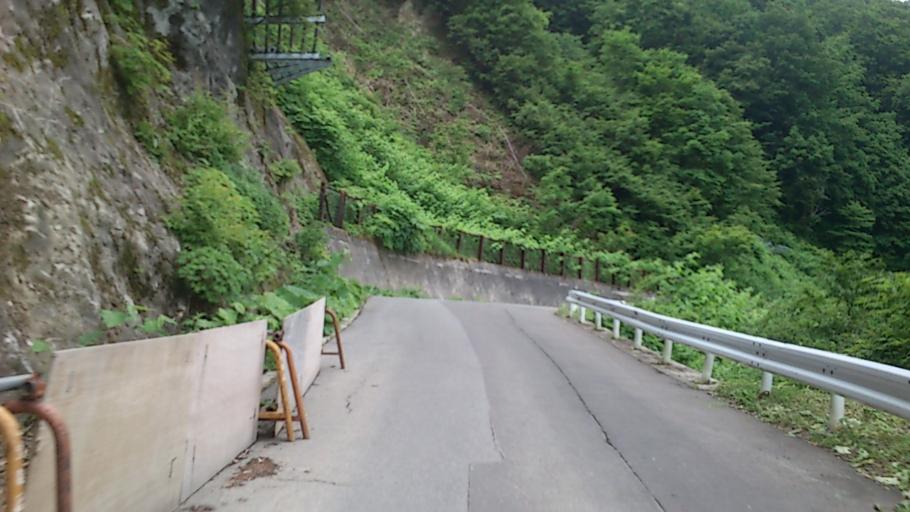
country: JP
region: Aomori
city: Hirosaki
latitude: 40.5201
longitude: 140.1772
